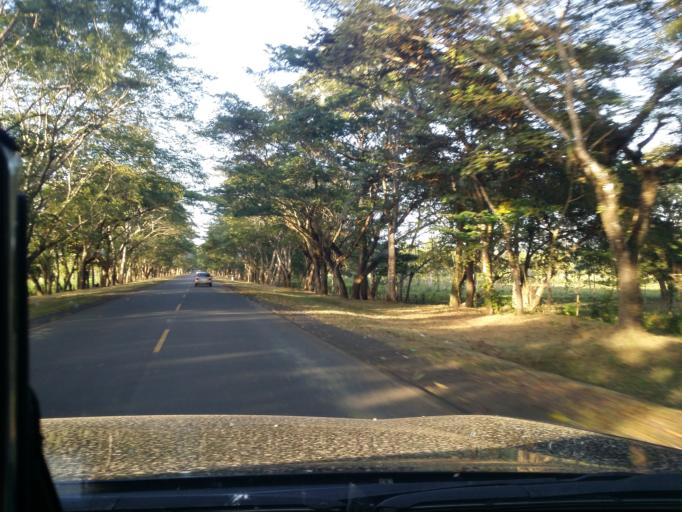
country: NI
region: Rio San Juan
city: San Miguelito
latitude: 11.4486
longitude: -84.8511
